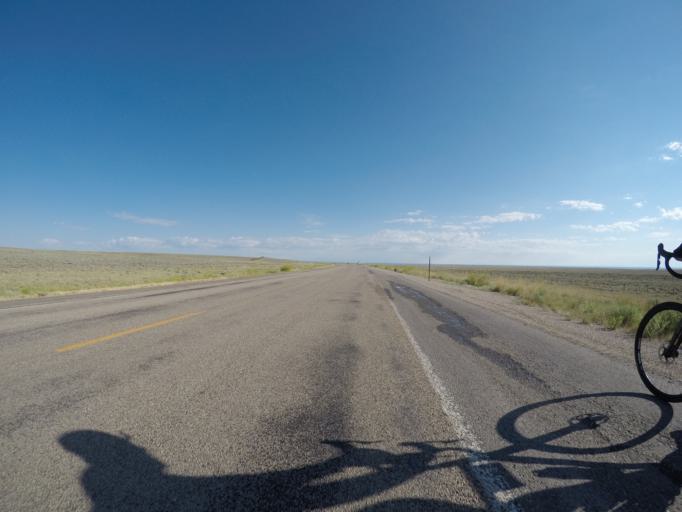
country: US
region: Wyoming
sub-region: Lincoln County
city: Kemmerer
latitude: 42.0262
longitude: -110.1525
